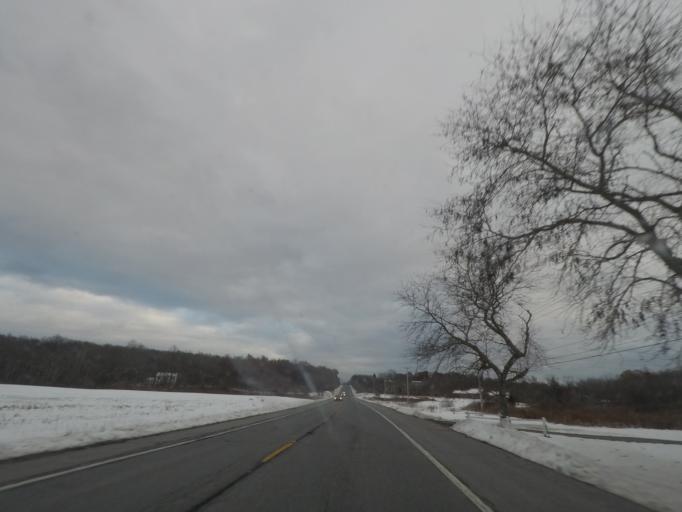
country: US
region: New York
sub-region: Ulster County
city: Plattekill
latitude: 41.6404
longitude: -74.1103
